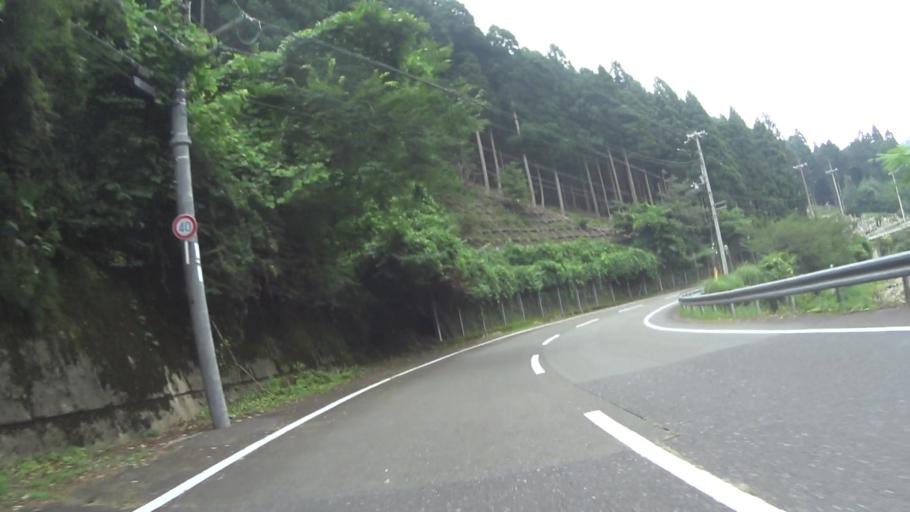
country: JP
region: Shiga Prefecture
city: Kitahama
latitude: 35.2039
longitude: 135.7660
